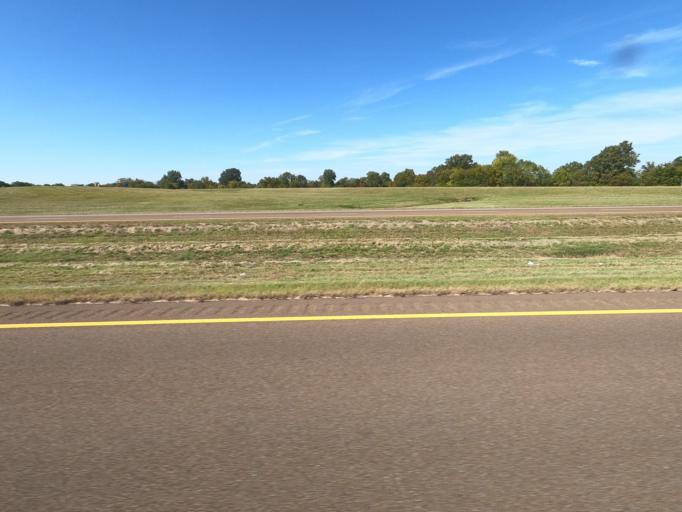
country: US
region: Tennessee
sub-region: Dyer County
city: Newbern
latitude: 36.1227
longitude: -89.2799
